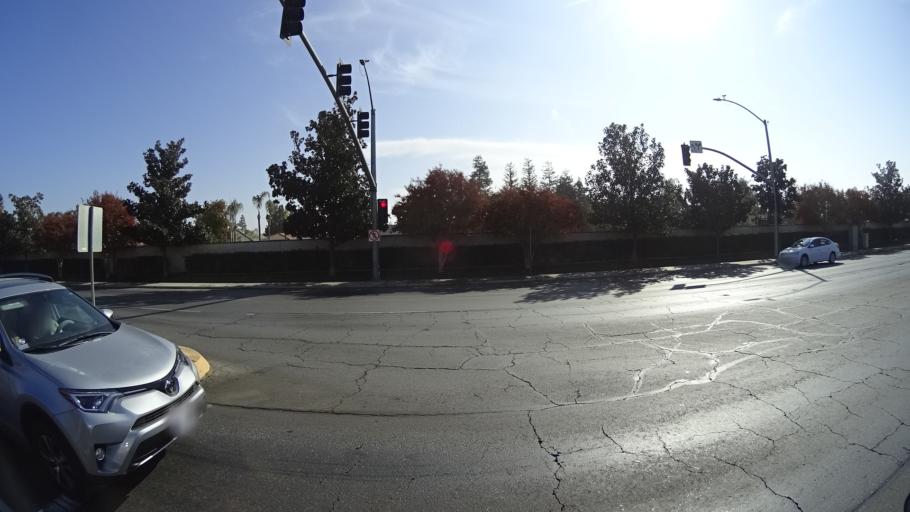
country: US
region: California
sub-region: Kern County
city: Greenacres
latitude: 35.3500
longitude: -119.1213
